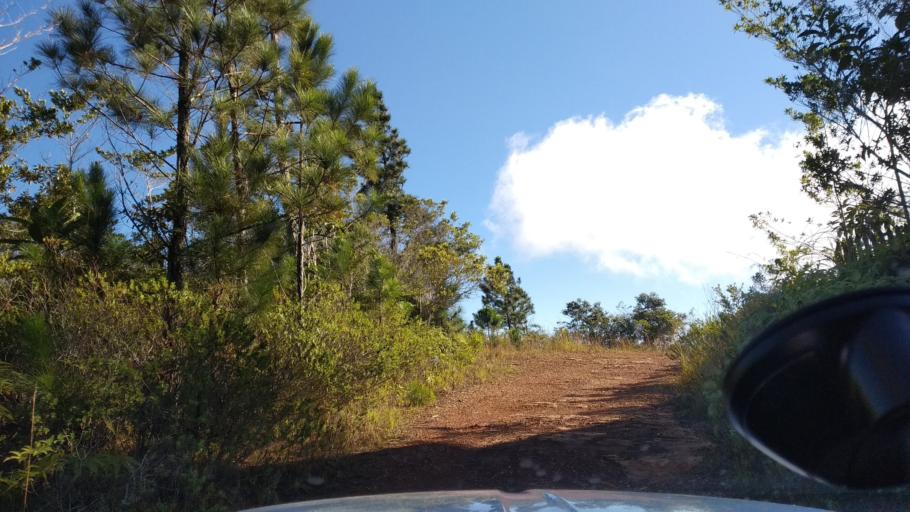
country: BZ
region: Cayo
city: Belmopan
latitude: 16.9985
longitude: -88.8484
